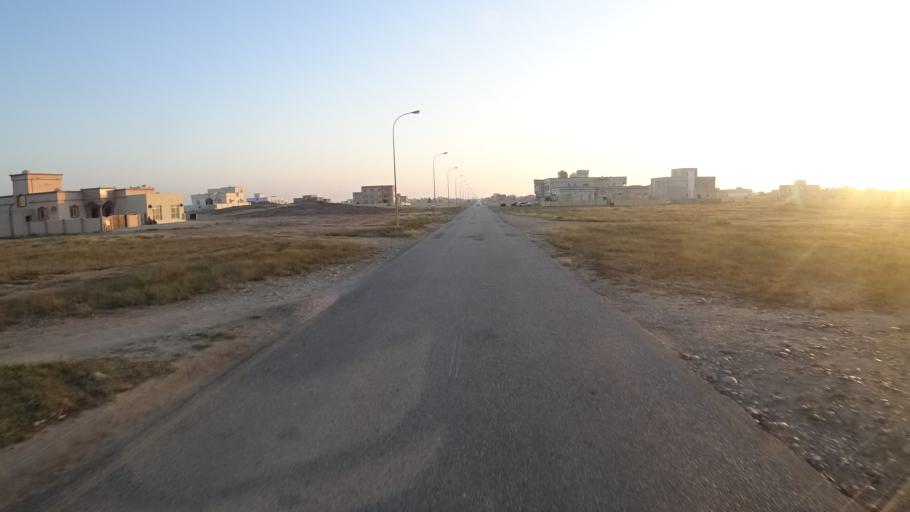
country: OM
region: Zufar
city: Salalah
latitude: 16.9934
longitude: 54.7192
